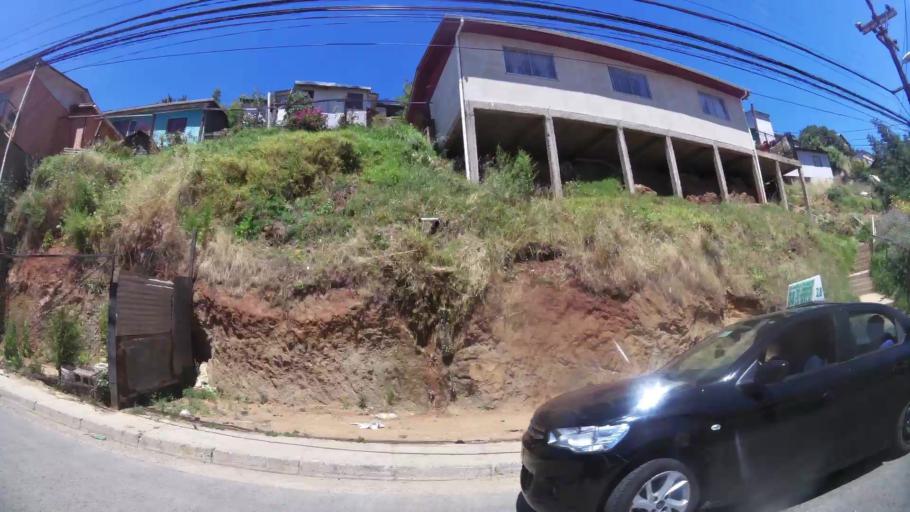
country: CL
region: Valparaiso
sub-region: Provincia de Valparaiso
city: Valparaiso
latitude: -33.0554
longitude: -71.6313
